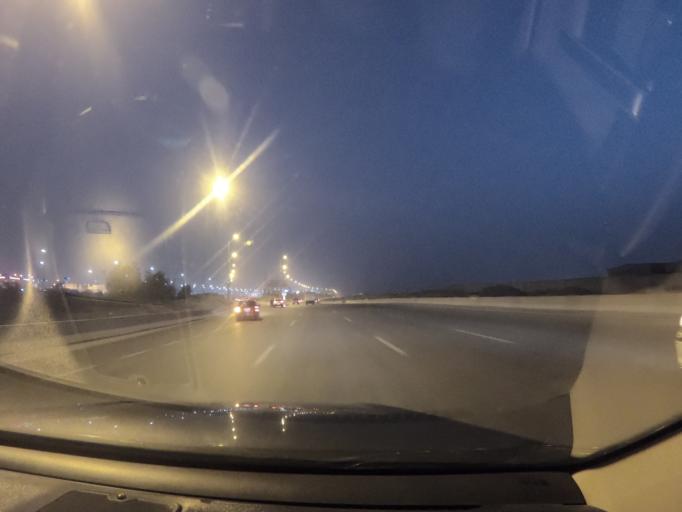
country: EG
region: Muhafazat al Qahirah
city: Cairo
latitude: 30.0328
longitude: 31.4022
